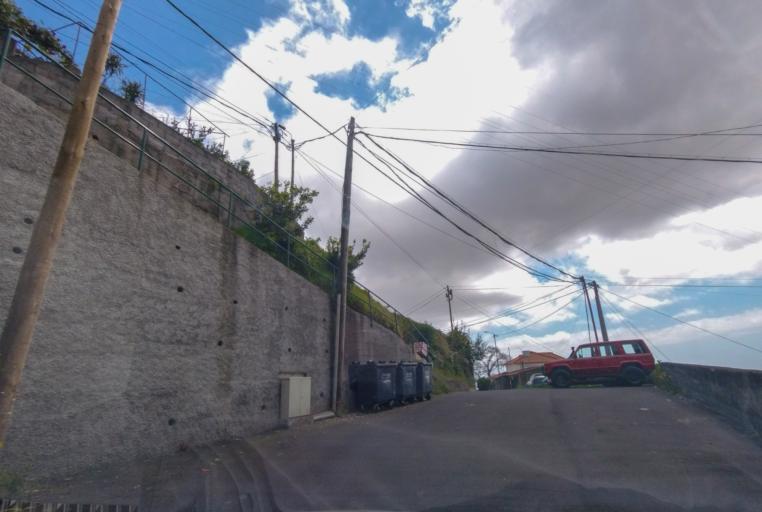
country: PT
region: Madeira
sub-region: Funchal
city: Nossa Senhora do Monte
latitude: 32.6811
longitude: -16.9120
